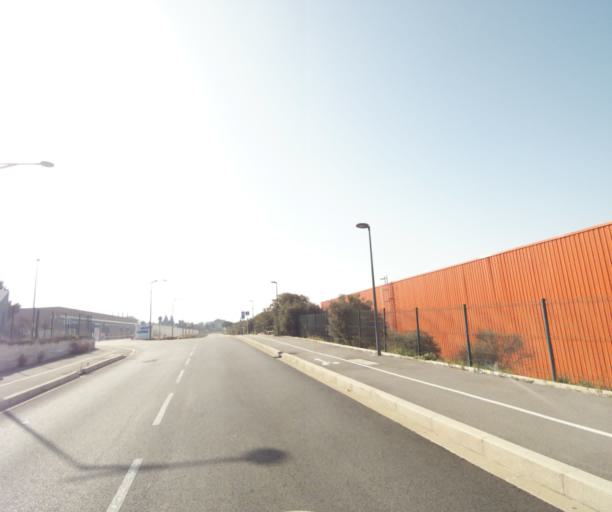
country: FR
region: Provence-Alpes-Cote d'Azur
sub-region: Departement des Bouches-du-Rhone
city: Vitrolles
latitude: 43.4435
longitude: 5.2345
